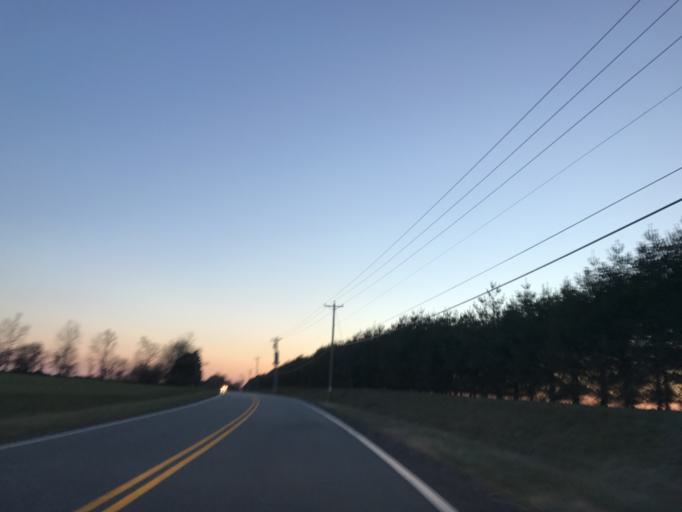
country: US
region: Maryland
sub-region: Queen Anne's County
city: Centreville
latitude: 39.0446
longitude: -76.0202
